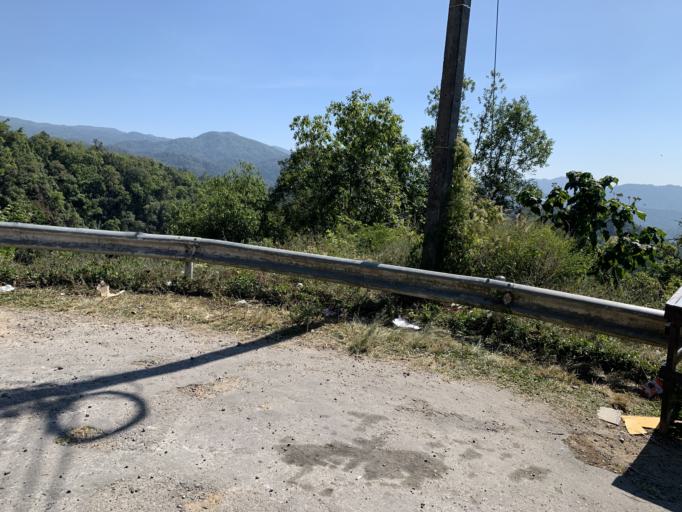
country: TH
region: Tak
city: Umphang
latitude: 16.2306
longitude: 98.9539
